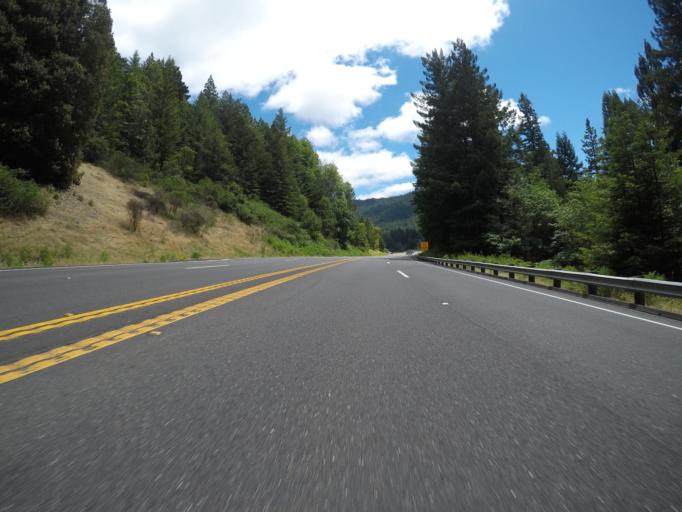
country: US
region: California
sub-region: Humboldt County
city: Redway
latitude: 40.2708
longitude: -123.8751
